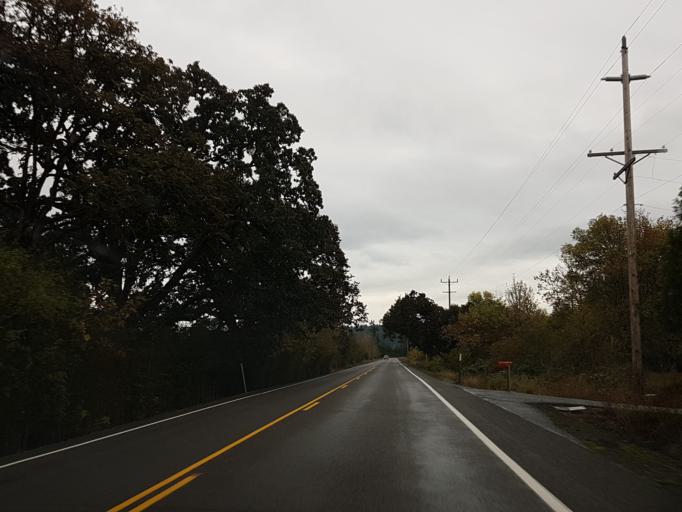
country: US
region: Oregon
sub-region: Marion County
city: Stayton
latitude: 44.7106
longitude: -122.7901
